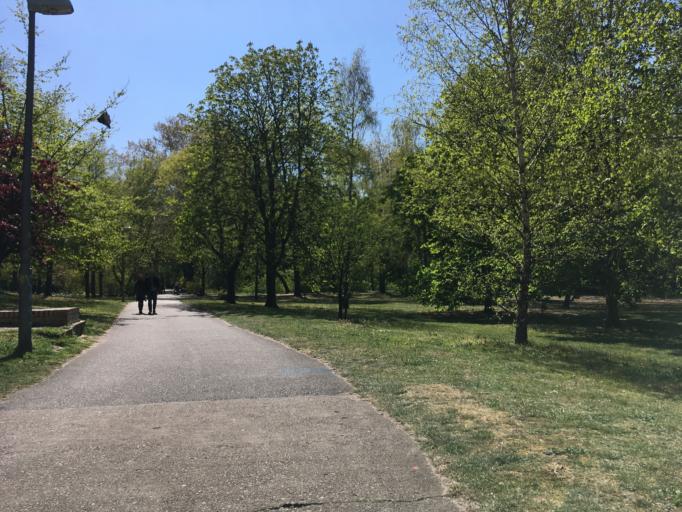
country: DE
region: Berlin
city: Friedrichsfelde
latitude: 52.5004
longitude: 13.5044
